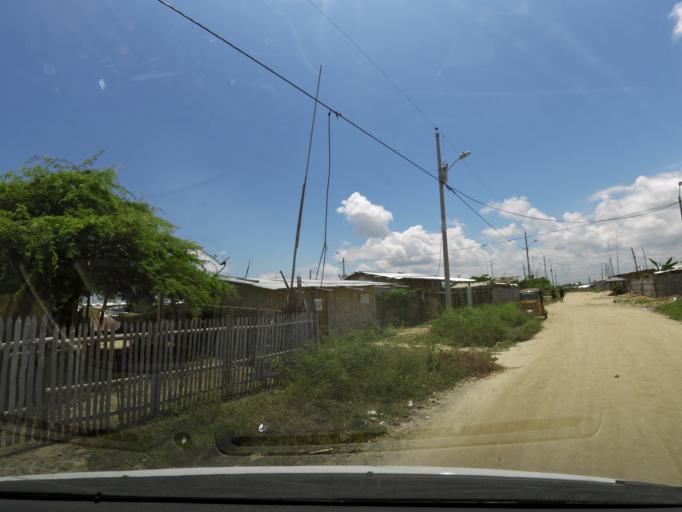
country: EC
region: El Oro
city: Huaquillas
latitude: -3.4734
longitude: -80.2100
